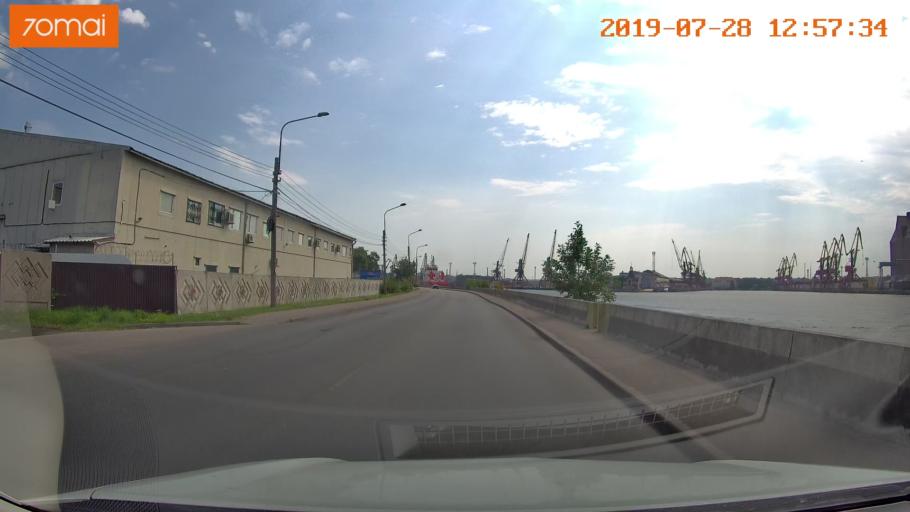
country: RU
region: Kaliningrad
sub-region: Gorod Kaliningrad
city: Kaliningrad
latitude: 54.7063
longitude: 20.4708
